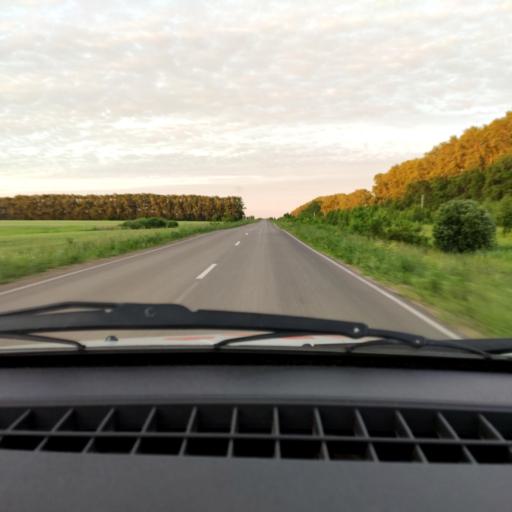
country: RU
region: Bashkortostan
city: Avdon
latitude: 54.5287
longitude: 55.7671
